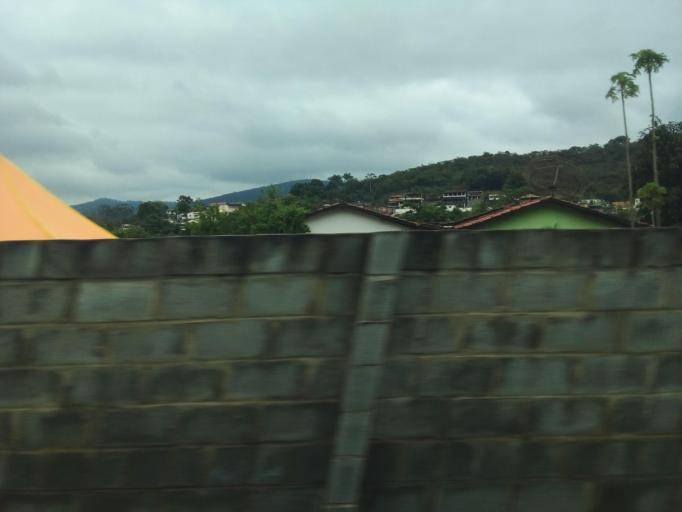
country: BR
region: Minas Gerais
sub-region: Rio Piracicaba
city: Rio Piracicaba
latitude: -19.9351
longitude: -43.1725
